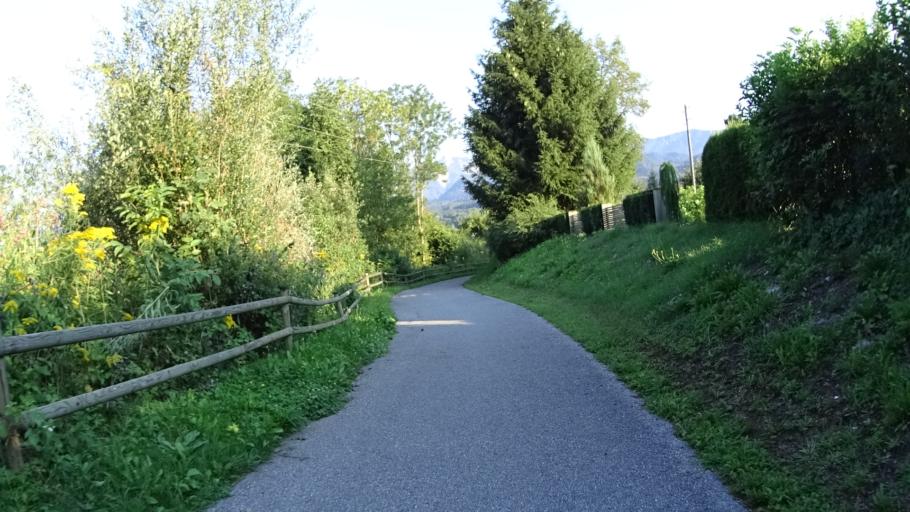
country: AT
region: Carinthia
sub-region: Politischer Bezirk Villach Land
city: Sankt Jakob
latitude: 46.5359
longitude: 14.0874
